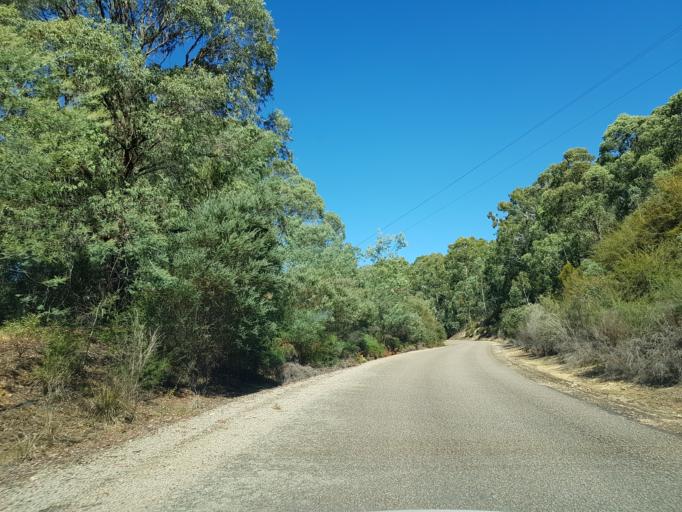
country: AU
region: Victoria
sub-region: Mansfield
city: Mansfield
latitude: -36.8963
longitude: 146.3865
